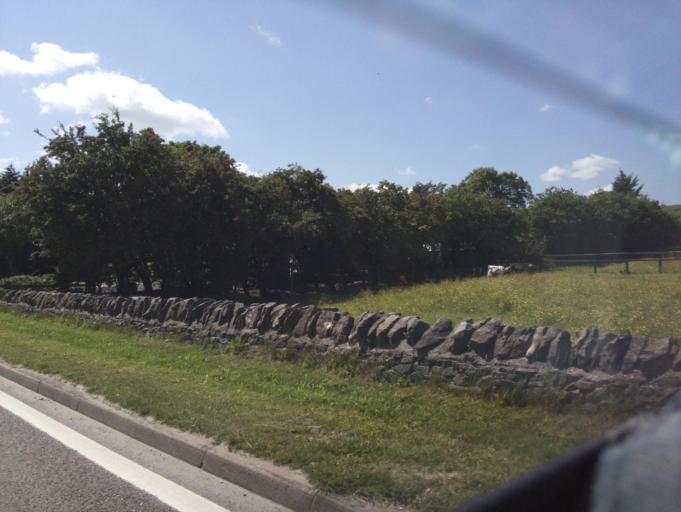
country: GB
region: England
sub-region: Derbyshire
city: Buxton
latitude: 53.2789
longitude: -1.8908
